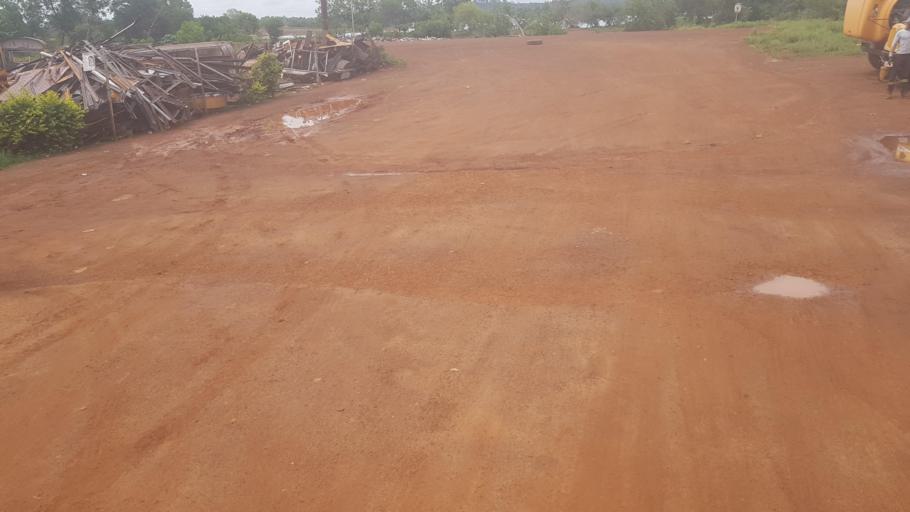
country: SL
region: Southern Province
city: Mogbwemo
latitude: 7.7574
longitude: -12.3046
